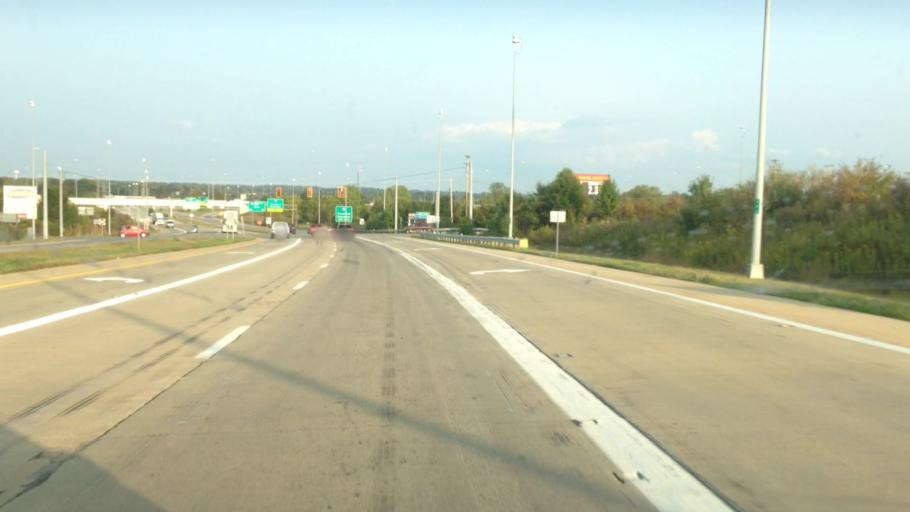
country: US
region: Ohio
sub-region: Medina County
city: Westfield Center
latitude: 41.0312
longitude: -81.9082
